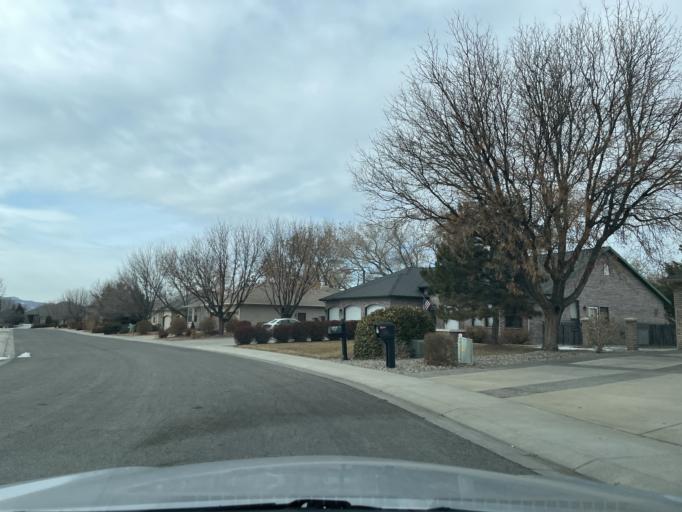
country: US
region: Colorado
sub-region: Mesa County
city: Grand Junction
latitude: 39.1051
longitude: -108.5822
